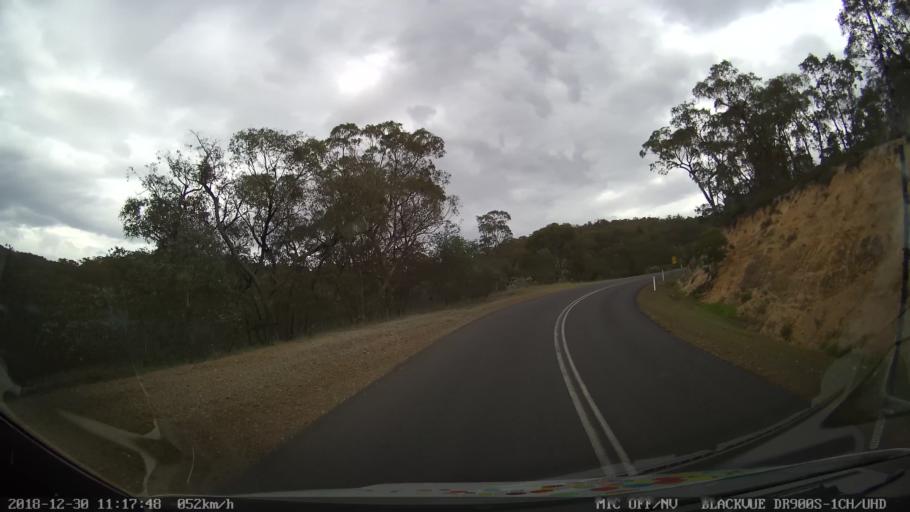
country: AU
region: New South Wales
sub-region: Snowy River
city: Jindabyne
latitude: -36.5363
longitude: 148.6956
